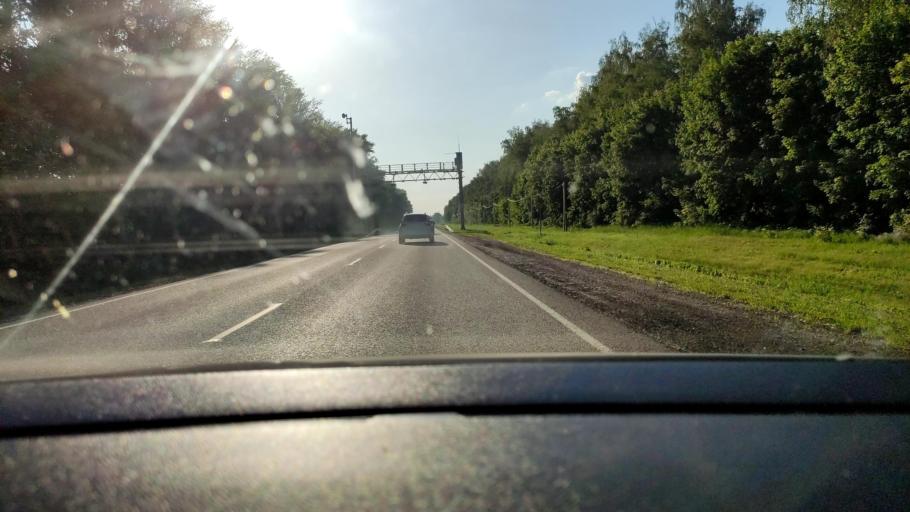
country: RU
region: Voronezj
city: Kashirskoye
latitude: 51.4706
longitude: 39.6951
